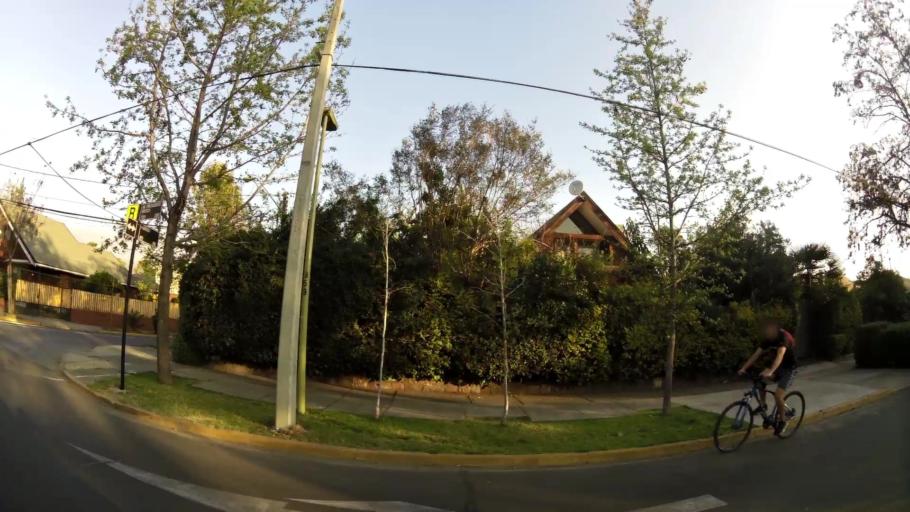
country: CL
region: Santiago Metropolitan
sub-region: Provincia de Santiago
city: Villa Presidente Frei, Nunoa, Santiago, Chile
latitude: -33.3964
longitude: -70.5581
